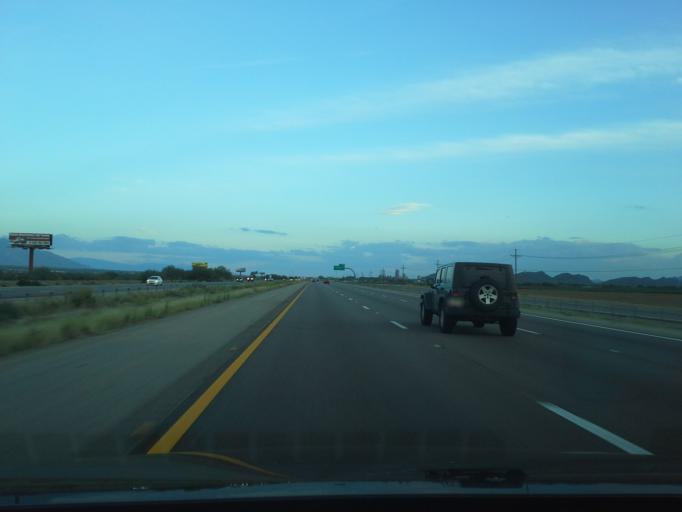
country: US
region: Arizona
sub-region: Pima County
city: Marana
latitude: 32.4342
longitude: -111.1774
